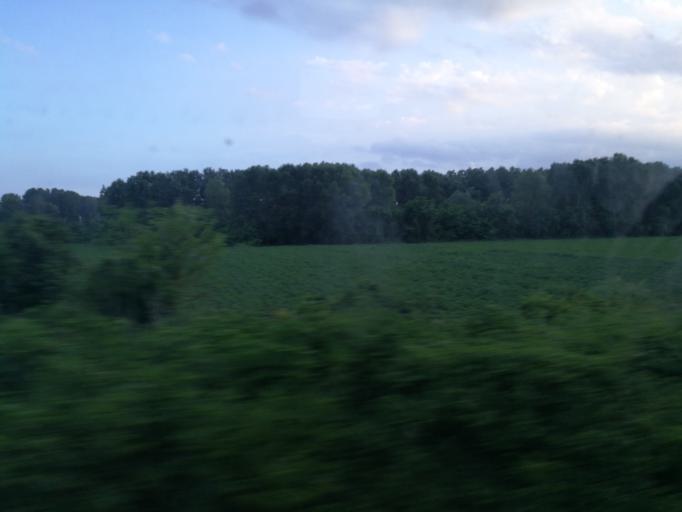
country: RO
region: Dambovita
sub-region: Comuna Contesti
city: Contesti
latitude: 44.6576
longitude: 25.6469
